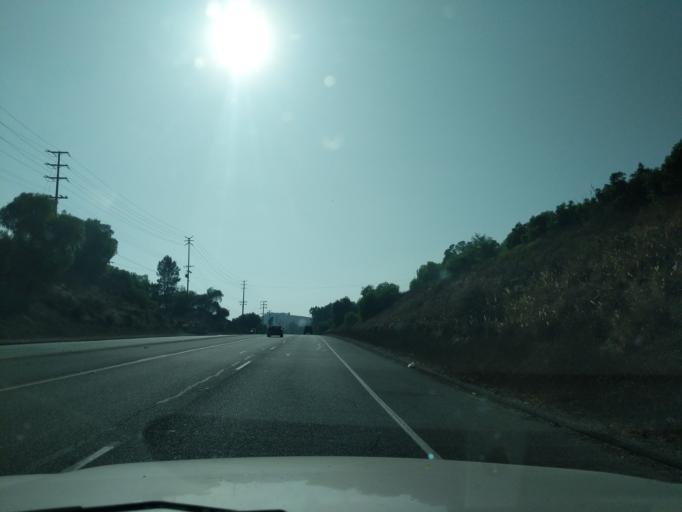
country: US
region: California
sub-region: Ventura County
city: Moorpark
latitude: 34.2686
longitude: -118.8380
